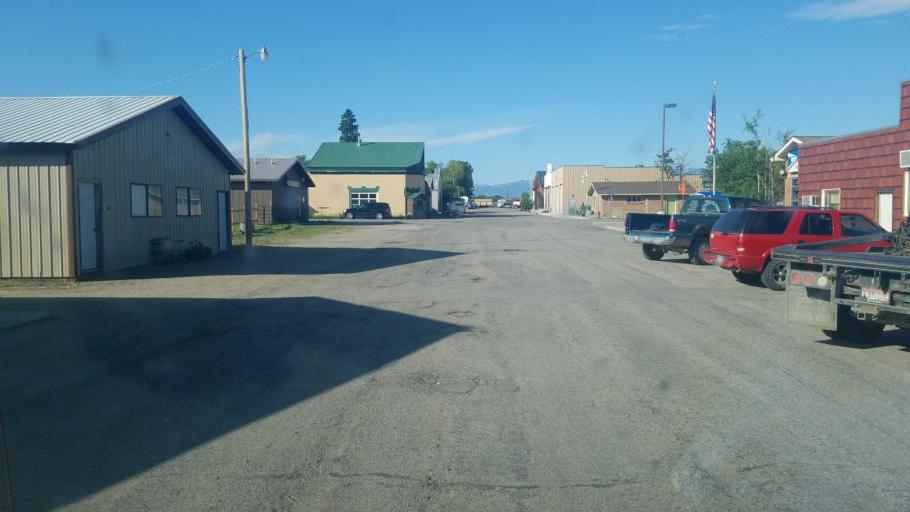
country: US
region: Montana
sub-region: Carbon County
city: Red Lodge
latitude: 45.3591
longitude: -109.1673
